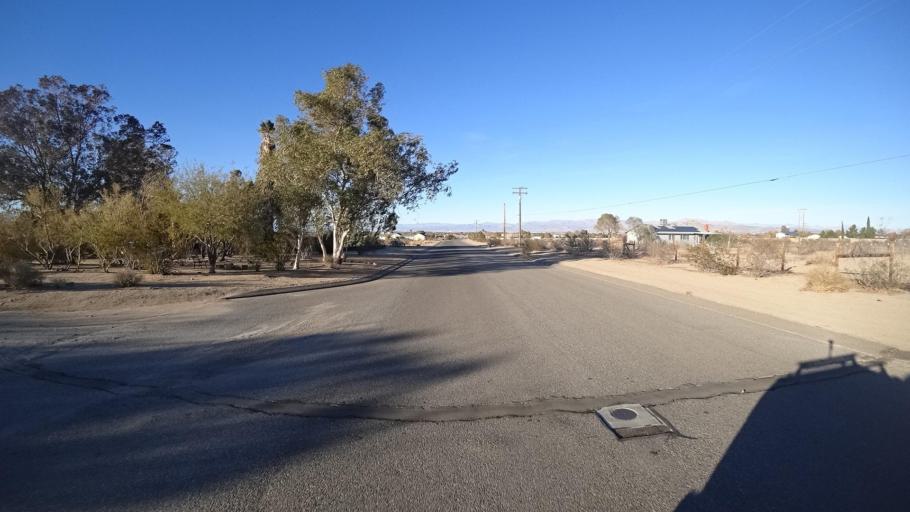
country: US
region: California
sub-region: Kern County
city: Ridgecrest
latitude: 35.5916
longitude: -117.6617
